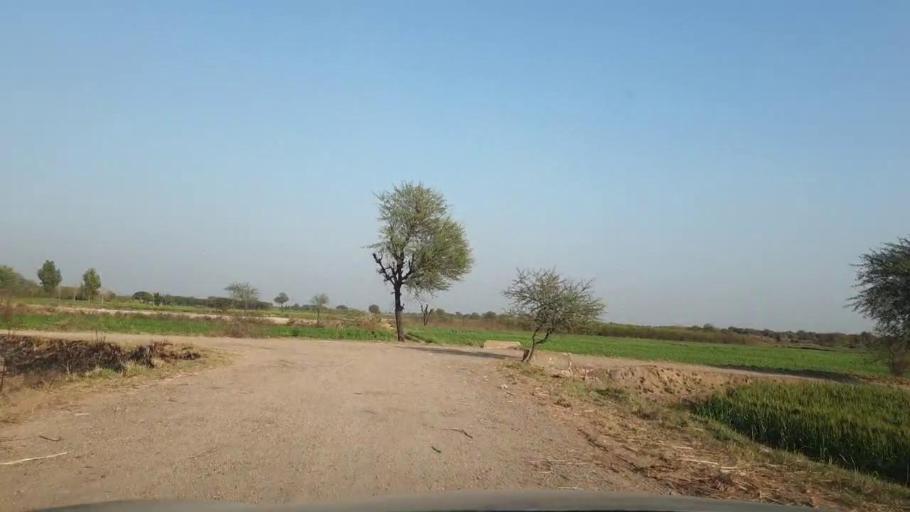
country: PK
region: Sindh
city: Tando Allahyar
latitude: 25.5864
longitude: 68.6758
